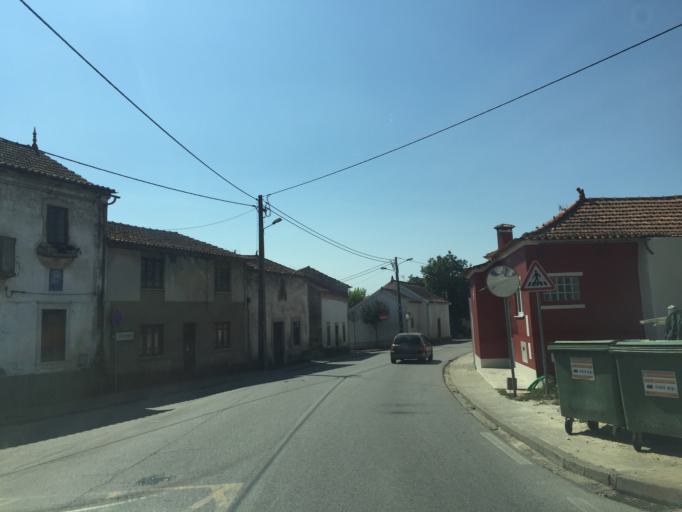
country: PT
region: Coimbra
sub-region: Cantanhede
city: Cantanhede
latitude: 40.3568
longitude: -8.5507
